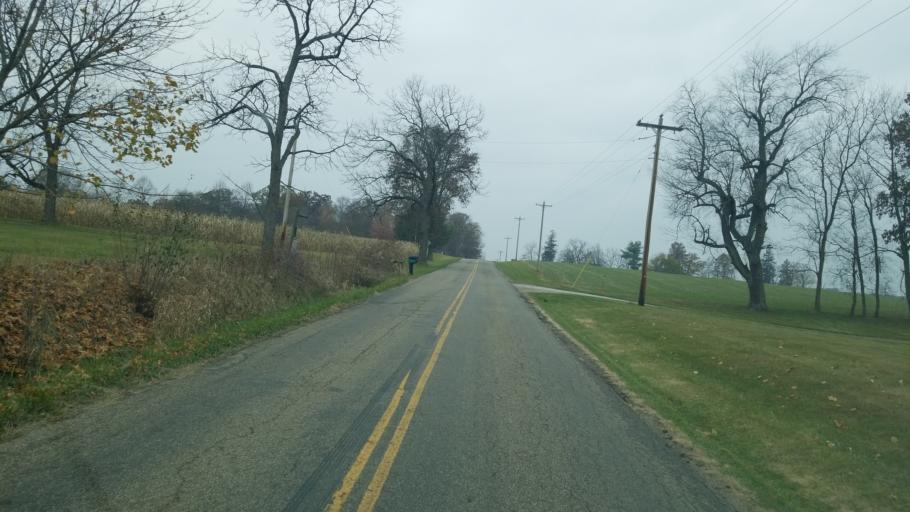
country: US
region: Ohio
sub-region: Knox County
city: Gambier
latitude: 40.3543
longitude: -82.4299
